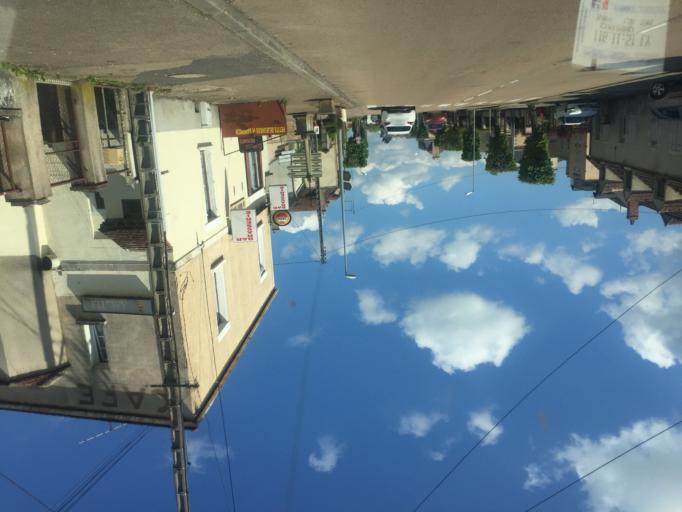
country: FR
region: Bourgogne
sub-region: Departement de l'Yonne
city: Avallon
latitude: 47.4922
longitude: 3.9198
